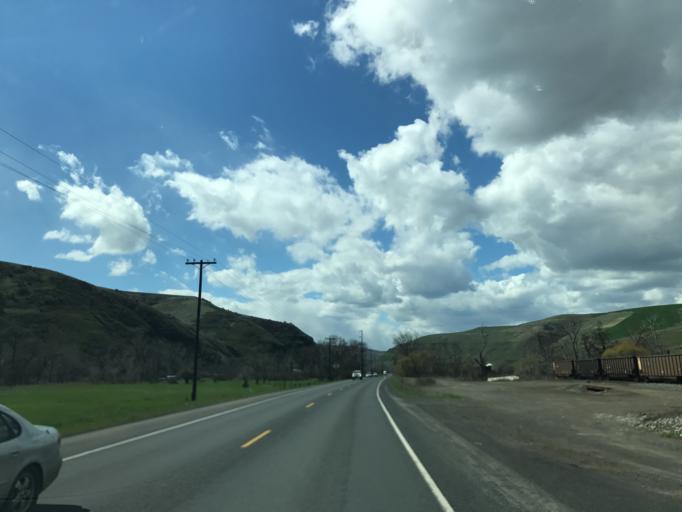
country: US
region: Idaho
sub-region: Nez Perce County
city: Lapwai
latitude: 46.3695
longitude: -116.7256
